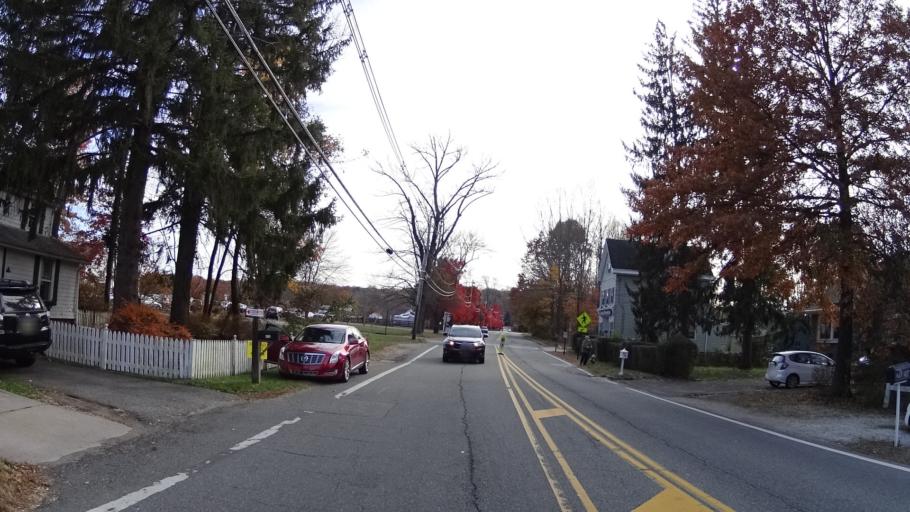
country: US
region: New Jersey
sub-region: Morris County
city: Morristown
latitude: 40.7779
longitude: -74.4669
